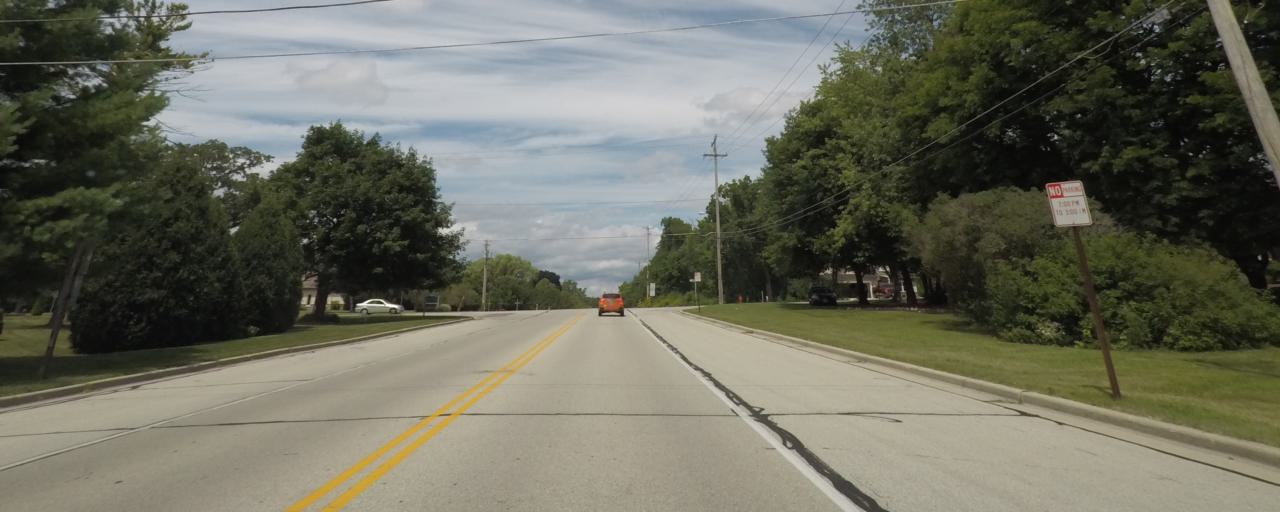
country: US
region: Wisconsin
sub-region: Milwaukee County
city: Hales Corners
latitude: 42.9657
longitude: -88.0691
